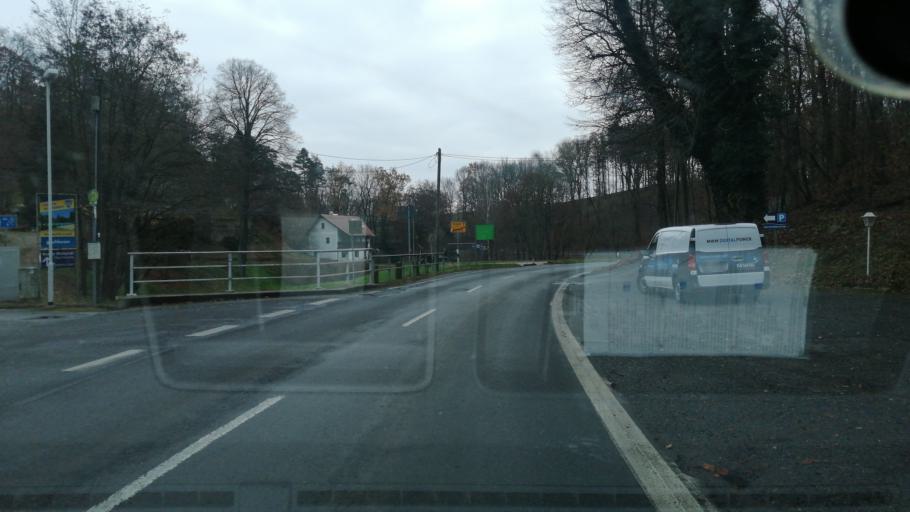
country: DE
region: Saxony
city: Bernstadt
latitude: 51.0605
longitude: 14.8085
